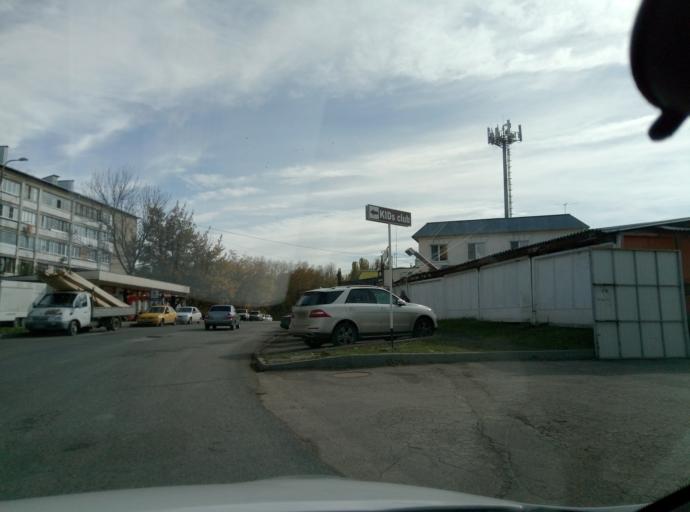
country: RU
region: Stavropol'skiy
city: Nezhinskiy
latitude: 43.9179
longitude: 42.7015
